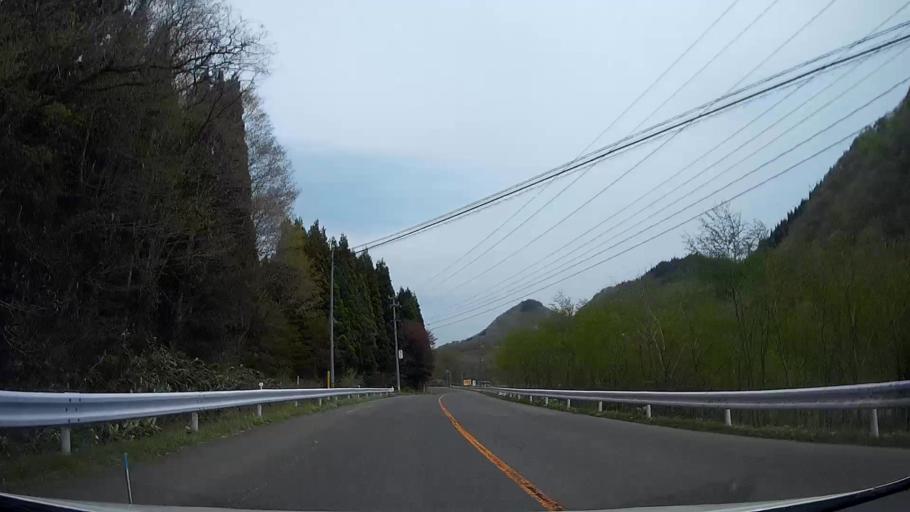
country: JP
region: Akita
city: Hanawa
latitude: 40.3653
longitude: 140.8610
